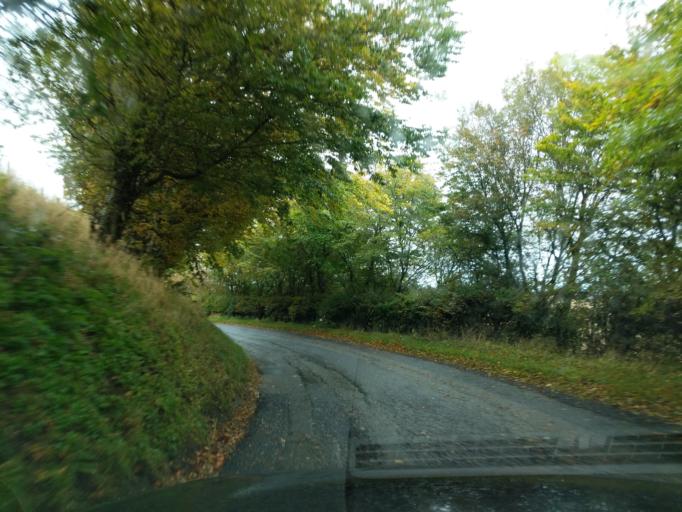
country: GB
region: Scotland
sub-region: East Lothian
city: Dunbar
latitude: 55.9487
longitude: -2.4183
